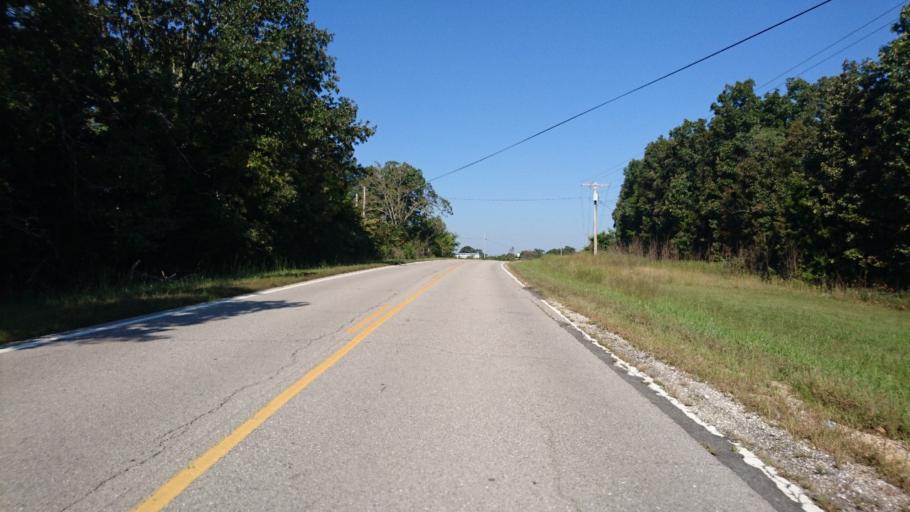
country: US
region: Missouri
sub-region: Pulaski County
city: Richland
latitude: 37.7454
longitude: -92.3571
